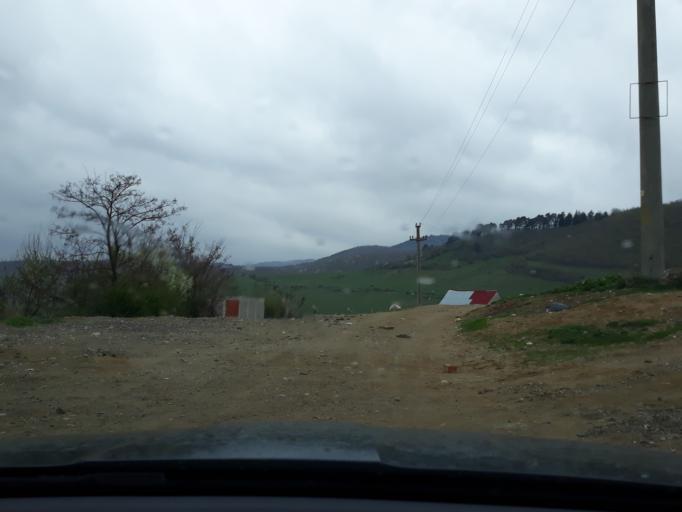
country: RO
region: Brasov
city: Codlea
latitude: 45.6937
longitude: 25.4363
